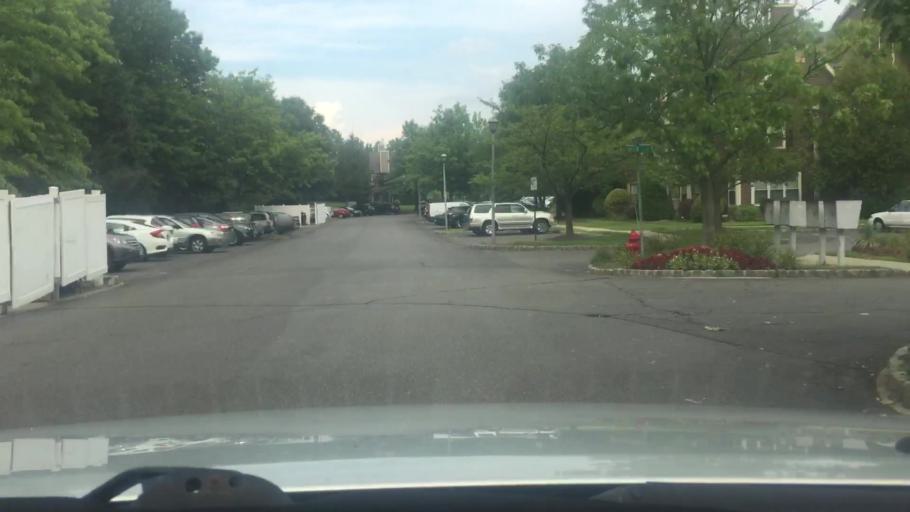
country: US
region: New Jersey
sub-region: Middlesex County
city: South River
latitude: 40.4582
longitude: -74.4053
